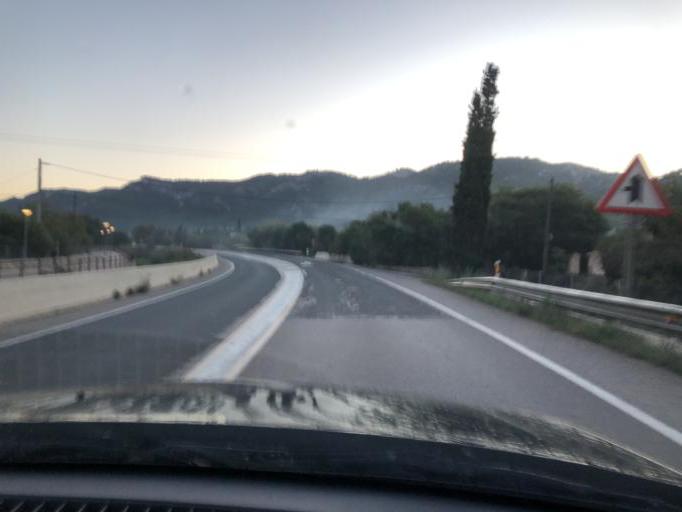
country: ES
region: Balearic Islands
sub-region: Illes Balears
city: Andratx
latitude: 39.5643
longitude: 2.4091
